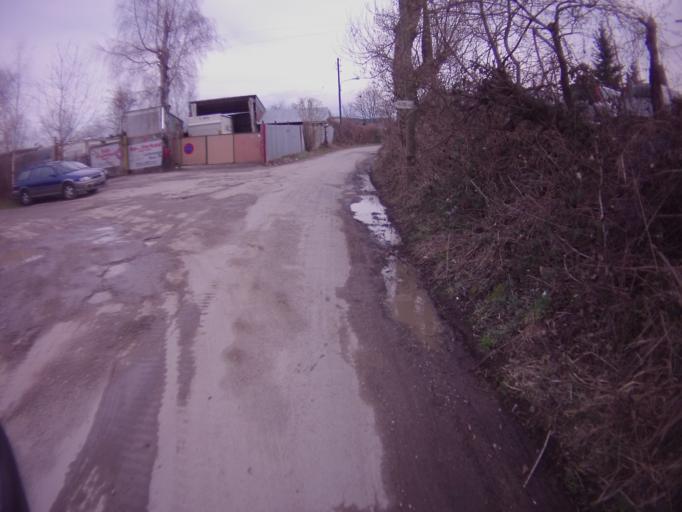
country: CH
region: Zurich
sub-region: Bezirk Dietikon
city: Dietikon / Almend
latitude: 47.4121
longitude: 8.3864
